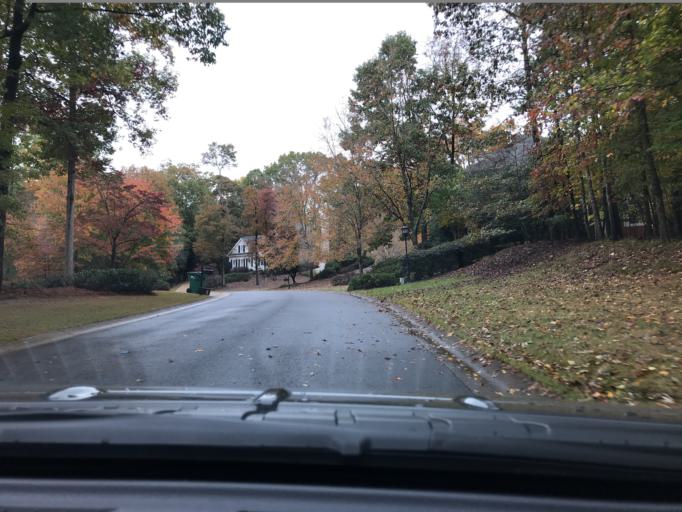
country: US
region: Georgia
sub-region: Fulton County
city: Johns Creek
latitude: 34.0049
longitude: -84.2324
